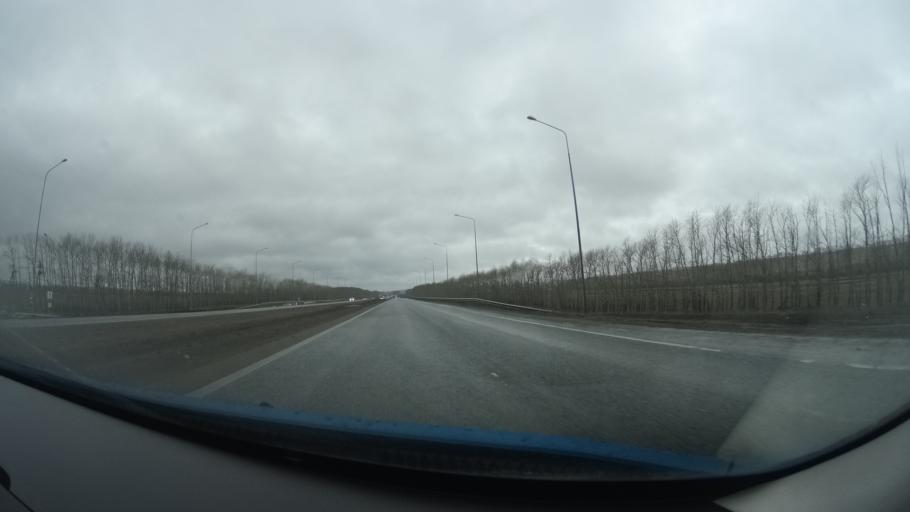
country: RU
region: Bashkortostan
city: Alekseyevka
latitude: 54.7294
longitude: 54.9925
